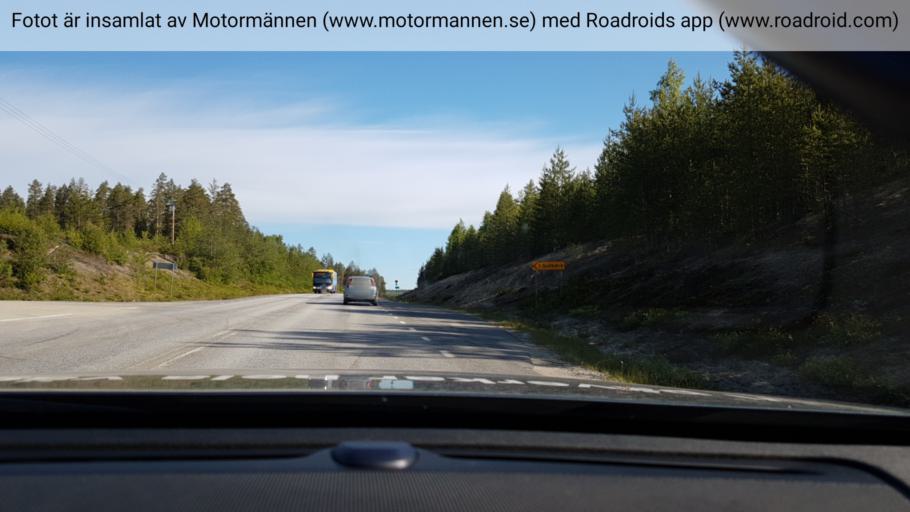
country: SE
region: Vaesterbotten
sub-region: Vannas Kommun
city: Vaennaes
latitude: 64.0301
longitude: 19.6923
